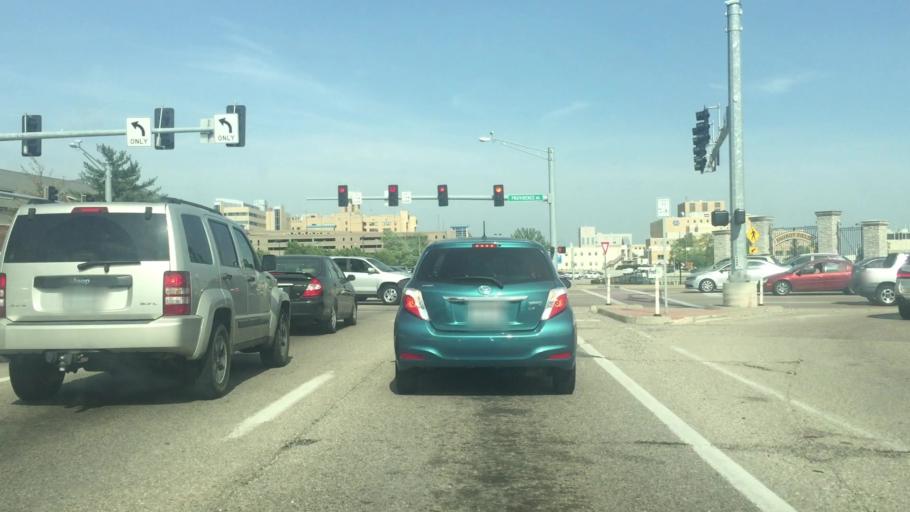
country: US
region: Missouri
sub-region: Boone County
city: Columbia
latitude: 38.9377
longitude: -92.3347
